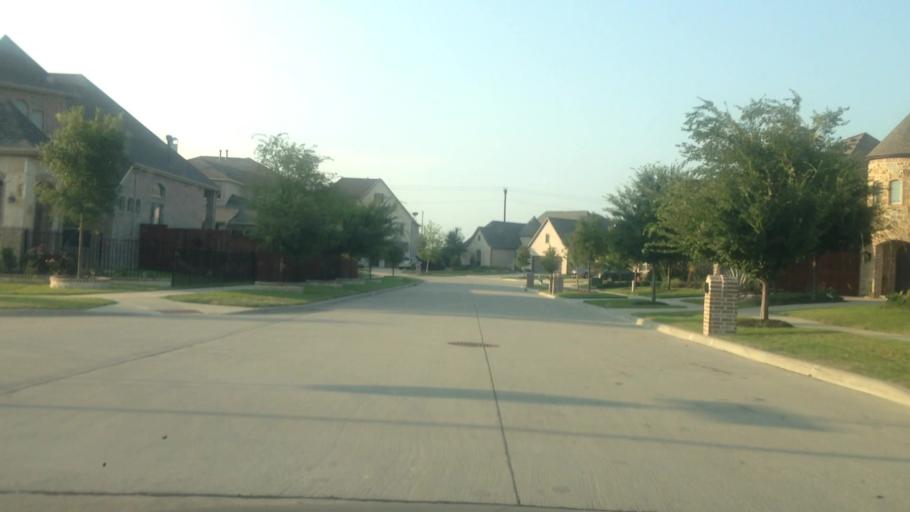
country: US
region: Texas
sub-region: Denton County
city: The Colony
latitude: 33.1314
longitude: -96.8665
